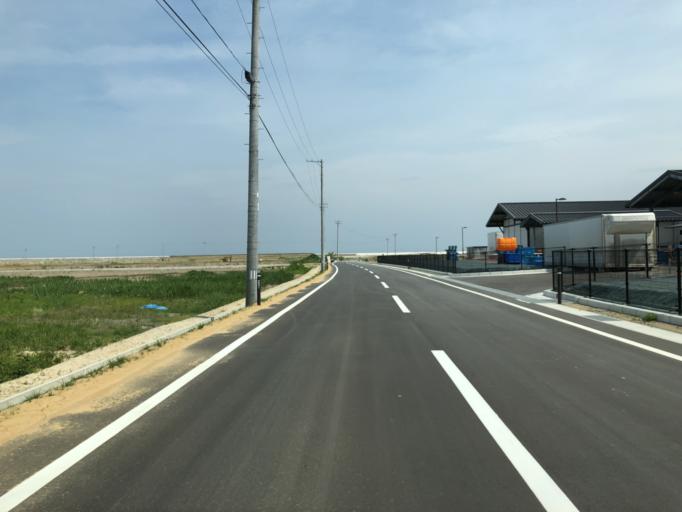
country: JP
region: Miyagi
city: Marumori
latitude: 37.7784
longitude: 140.9786
